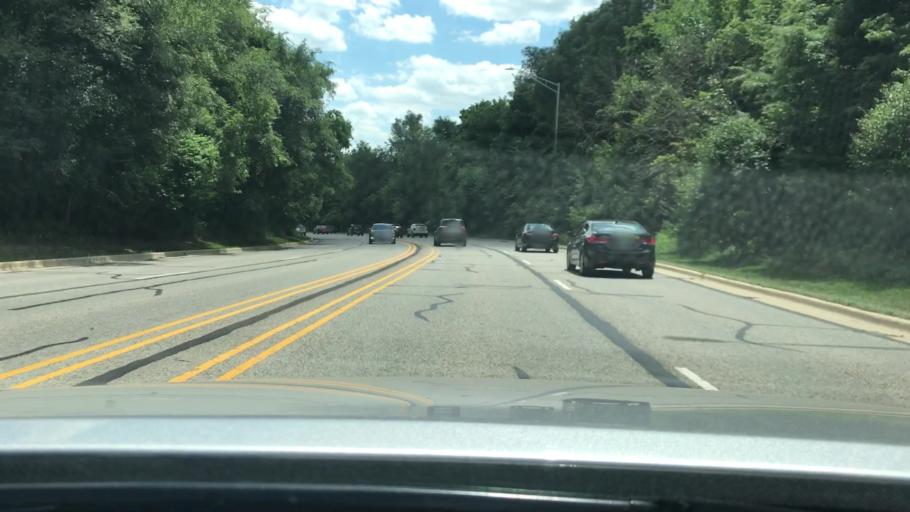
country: US
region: Illinois
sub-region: DuPage County
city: Naperville
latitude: 41.7890
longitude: -88.1173
